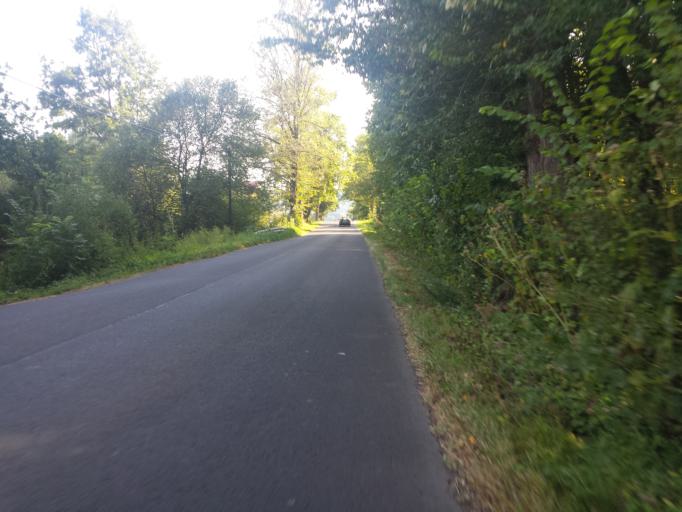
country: PL
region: Subcarpathian Voivodeship
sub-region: Powiat leski
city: Uherce Mineralne
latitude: 49.4555
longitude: 22.3915
